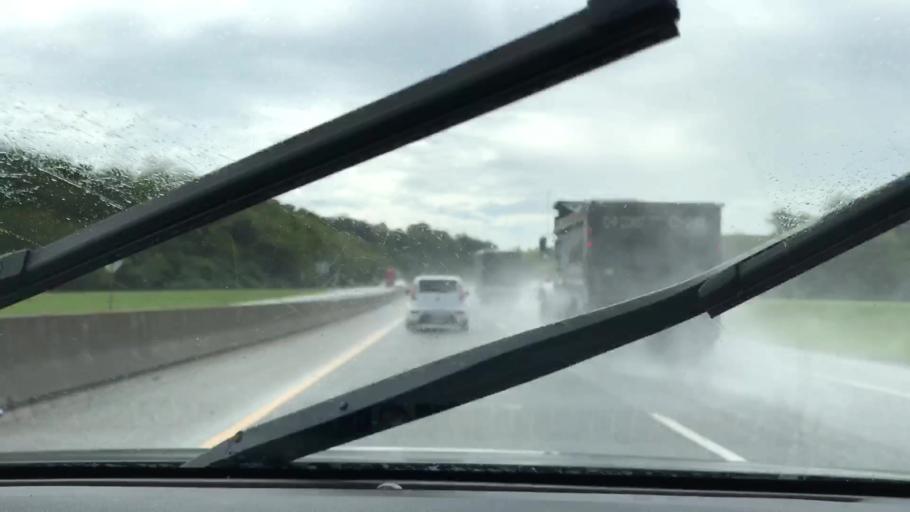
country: US
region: Tennessee
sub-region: Smith County
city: South Carthage
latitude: 36.2346
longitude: -85.9459
